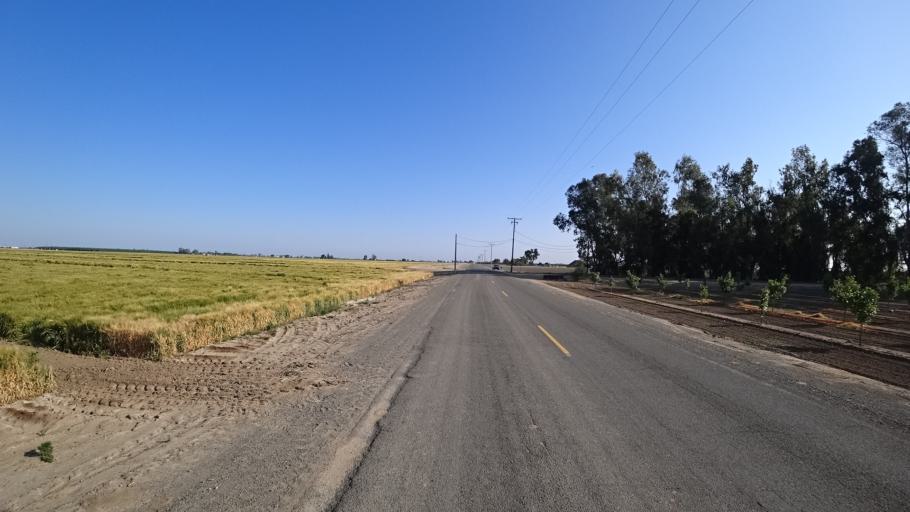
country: US
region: California
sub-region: Kings County
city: Home Garden
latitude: 36.3014
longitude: -119.5652
